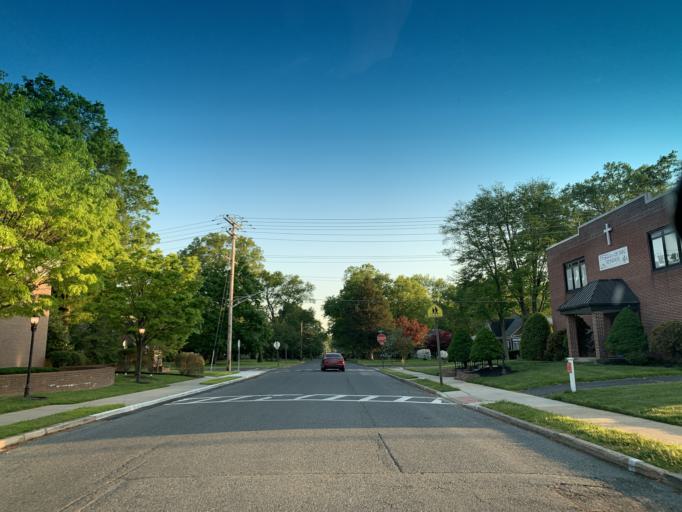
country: US
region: Maryland
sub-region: Harford County
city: Aberdeen
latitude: 39.5074
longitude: -76.1705
